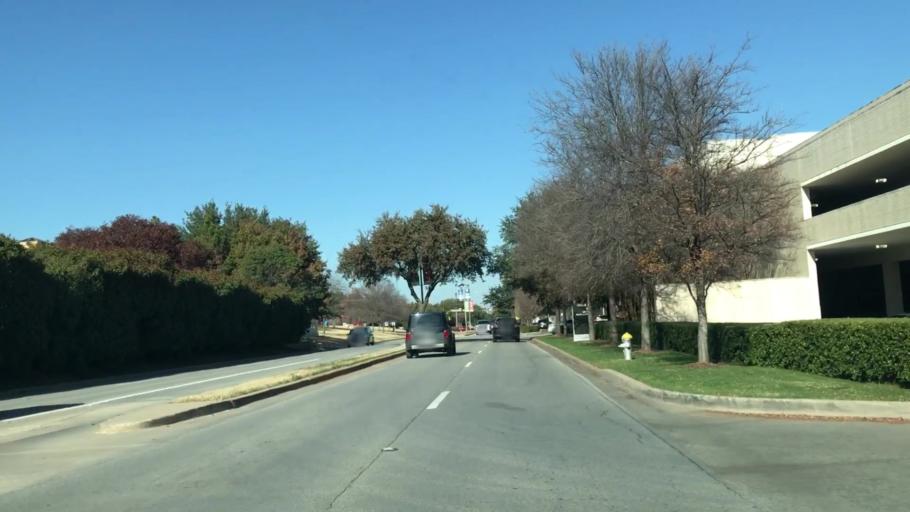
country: US
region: Texas
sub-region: Dallas County
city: University Park
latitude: 32.8696
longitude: -96.7764
